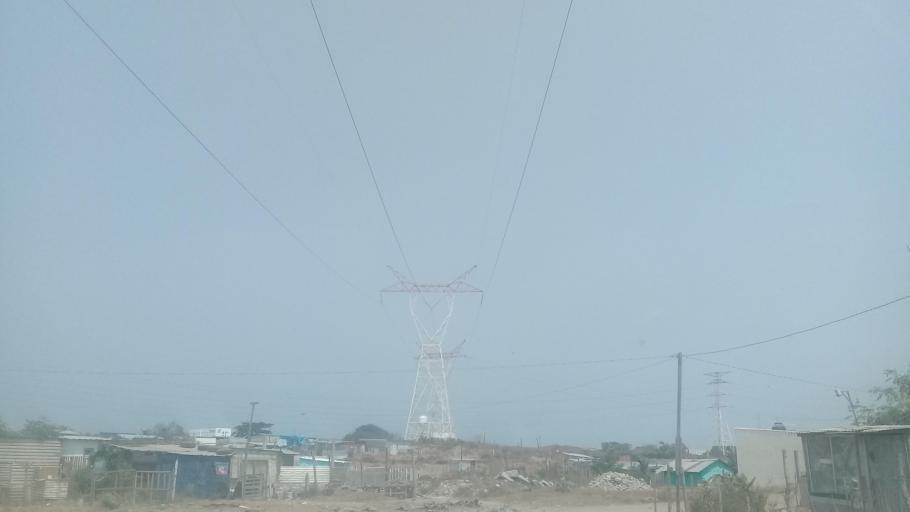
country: MX
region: Veracruz
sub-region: Veracruz
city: Las Amapolas
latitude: 19.1693
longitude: -96.1798
